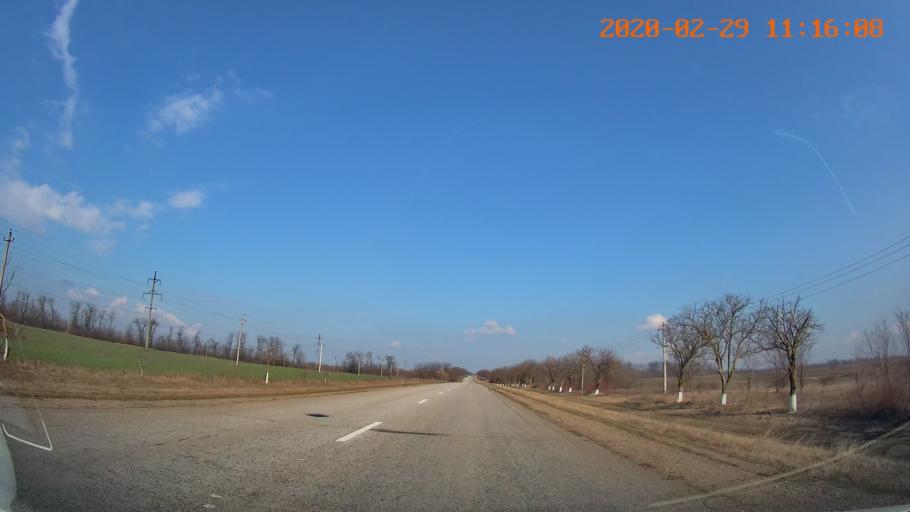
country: MD
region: Telenesti
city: Dubasari
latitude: 47.3043
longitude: 29.1670
